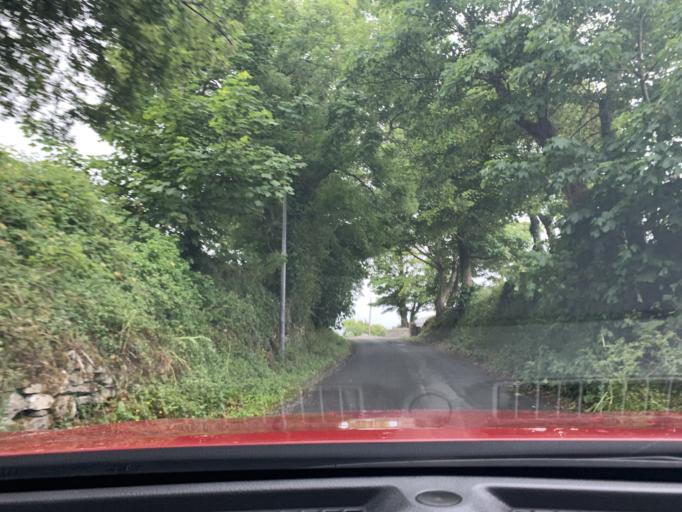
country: IE
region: Connaught
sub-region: Sligo
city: Sligo
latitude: 54.3130
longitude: -8.4774
